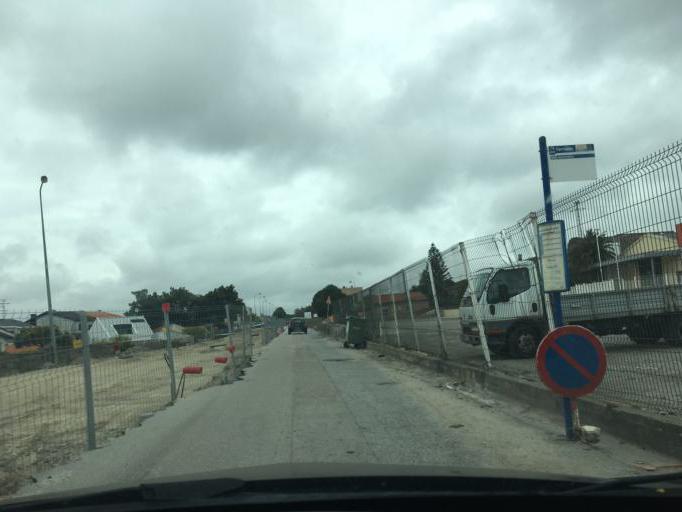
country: PT
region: Porto
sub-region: Matosinhos
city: Santa Cruz do Bispo
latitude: 41.2246
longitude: -8.6827
